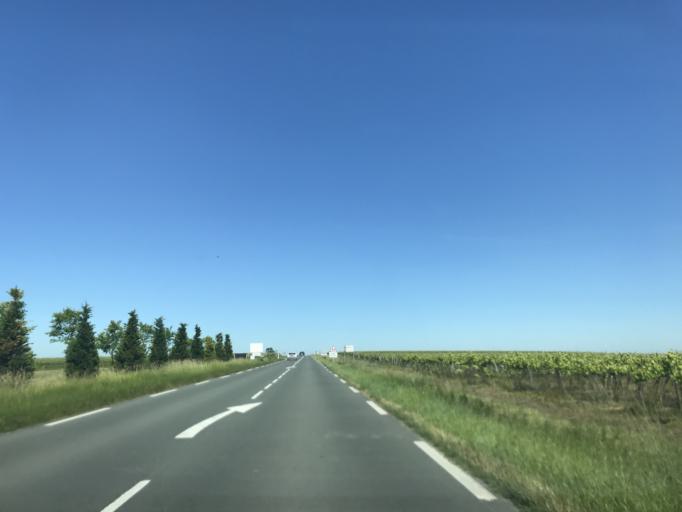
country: FR
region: Poitou-Charentes
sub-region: Departement de la Charente
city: Chateaubernard
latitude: 45.5504
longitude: -0.3625
